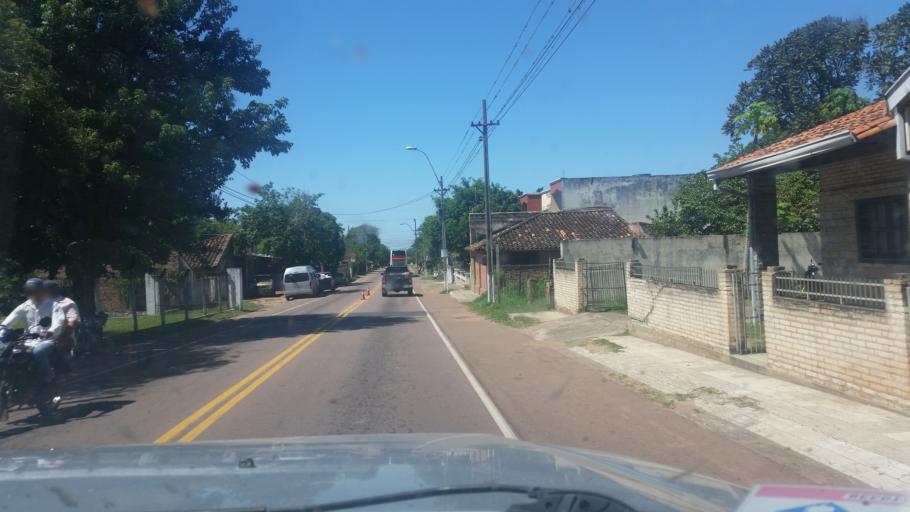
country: PY
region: Paraguari
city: Caapucu
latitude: -26.2339
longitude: -57.1795
